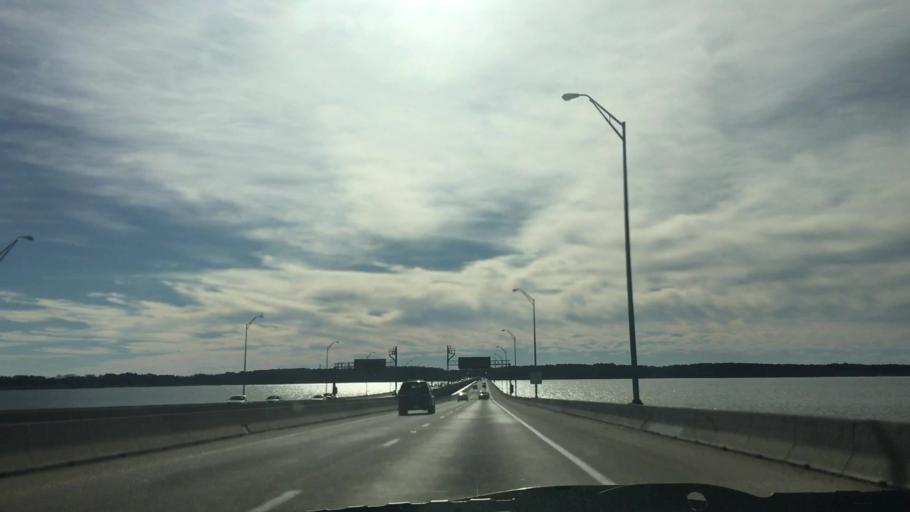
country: US
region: Virginia
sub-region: City of Newport News
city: Newport News
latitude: 36.9096
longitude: -76.4061
